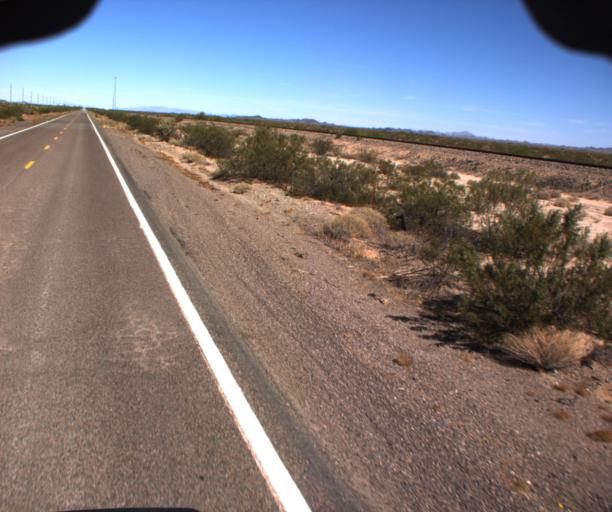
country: US
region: Arizona
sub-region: La Paz County
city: Salome
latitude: 33.8295
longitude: -113.8744
